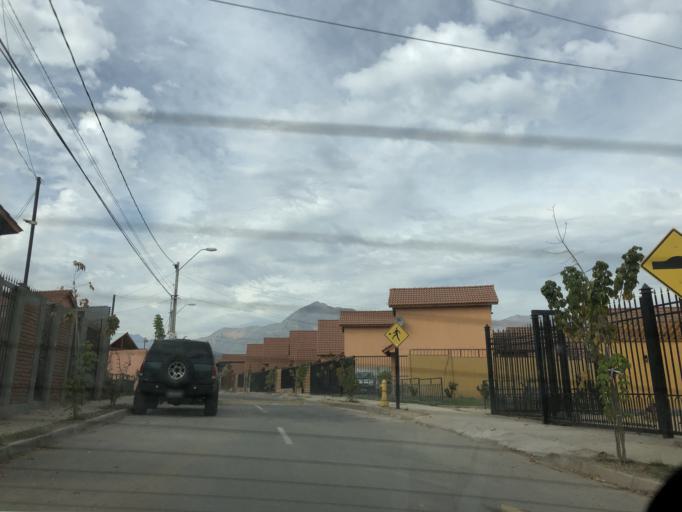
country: CL
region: Santiago Metropolitan
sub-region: Provincia de Cordillera
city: Puente Alto
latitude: -33.5866
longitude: -70.5313
